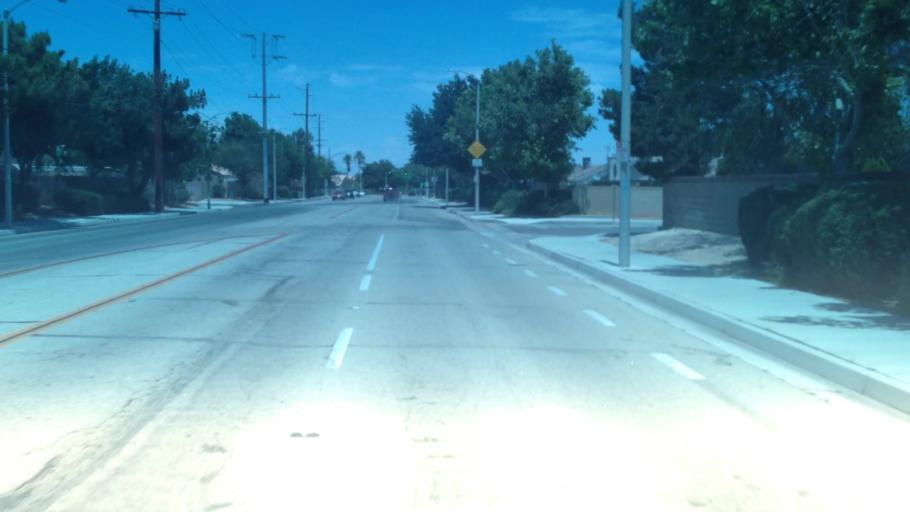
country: US
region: California
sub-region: Los Angeles County
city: Lancaster
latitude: 34.6871
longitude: -118.1747
